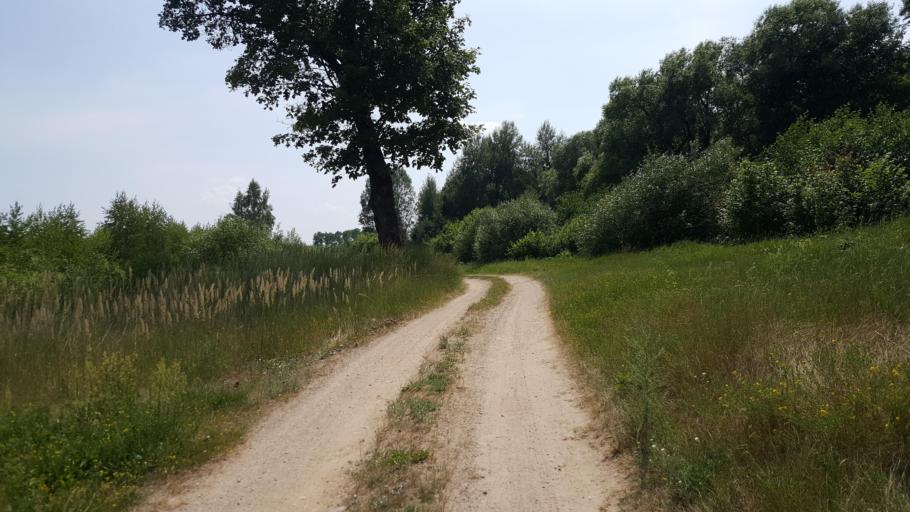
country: BY
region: Brest
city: Kamyanyets
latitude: 52.3652
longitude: 23.7444
